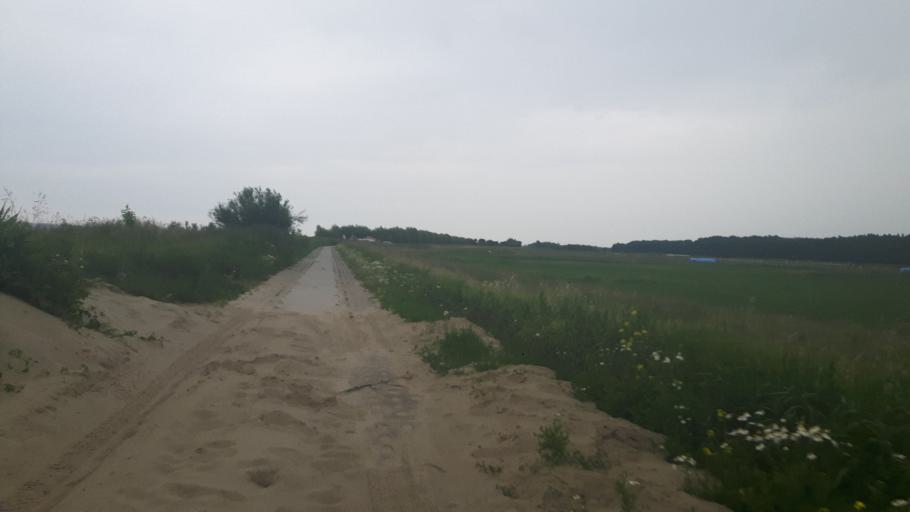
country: PL
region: Warmian-Masurian Voivodeship
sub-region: Powiat elblaski
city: Tolkmicko
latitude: 54.3006
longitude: 19.4691
